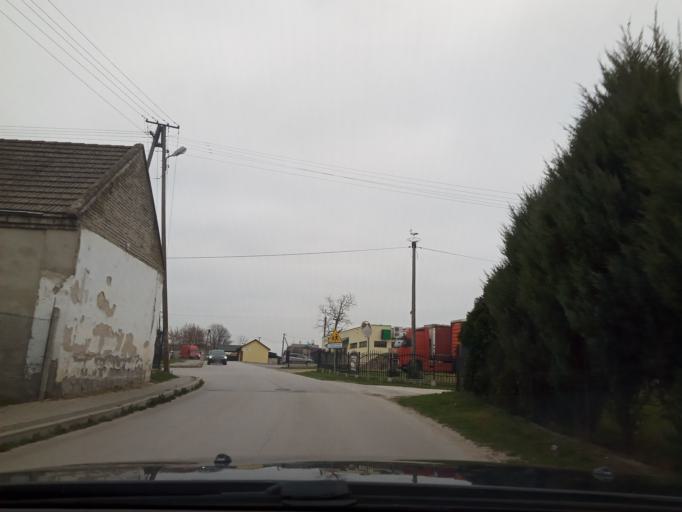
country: PL
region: Swietokrzyskie
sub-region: Powiat jedrzejowski
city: Imielno
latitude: 50.6028
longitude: 20.4910
